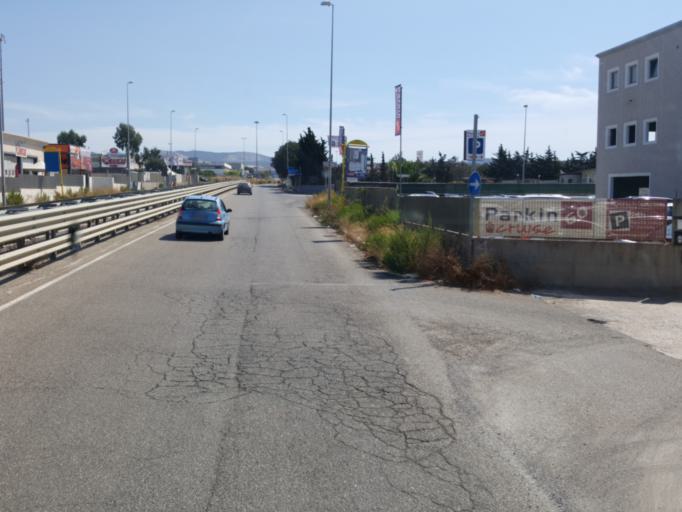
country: IT
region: Latium
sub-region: Citta metropolitana di Roma Capitale
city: Aurelia
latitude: 42.1199
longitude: 11.7751
